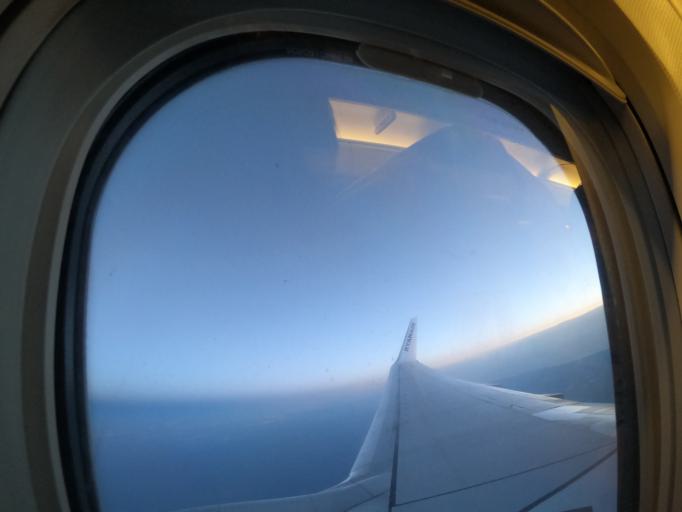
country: FR
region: Nord-Pas-de-Calais
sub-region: Departement du Nord
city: Ghyvelde
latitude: 51.0380
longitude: 2.5696
